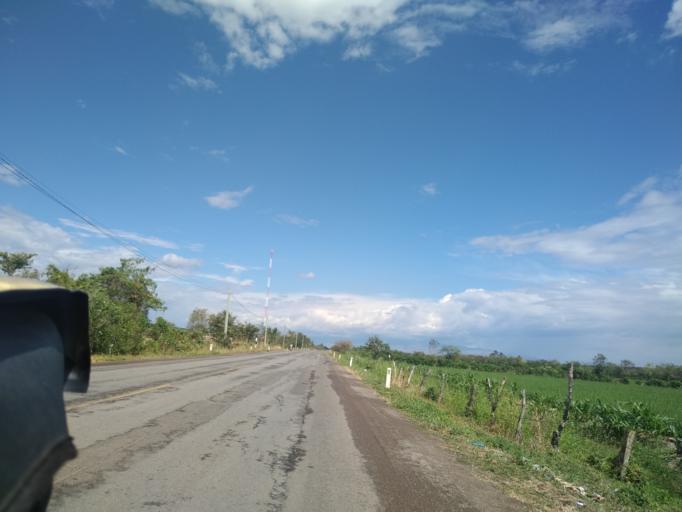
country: PE
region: Cajamarca
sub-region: Provincia de Jaen
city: Las Pirias
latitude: -5.5794
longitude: -78.8023
